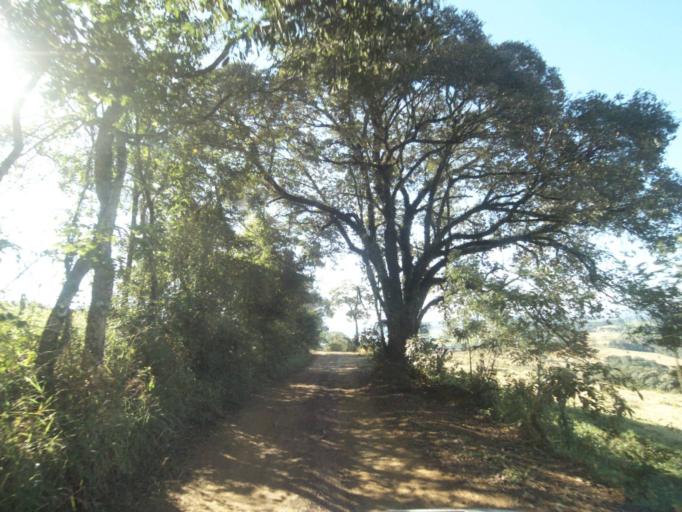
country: BR
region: Parana
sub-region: Tibagi
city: Tibagi
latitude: -24.5416
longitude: -50.4684
